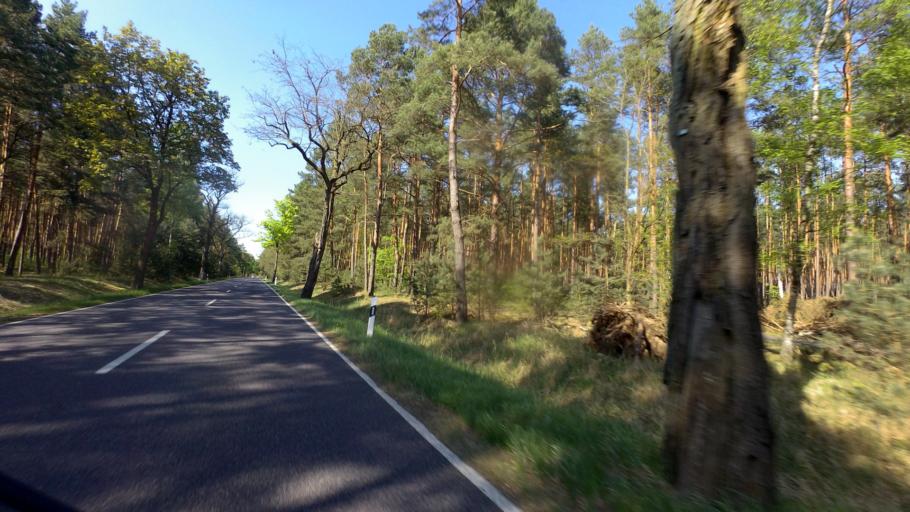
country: DE
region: Brandenburg
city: Halbe
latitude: 52.1417
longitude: 13.7482
